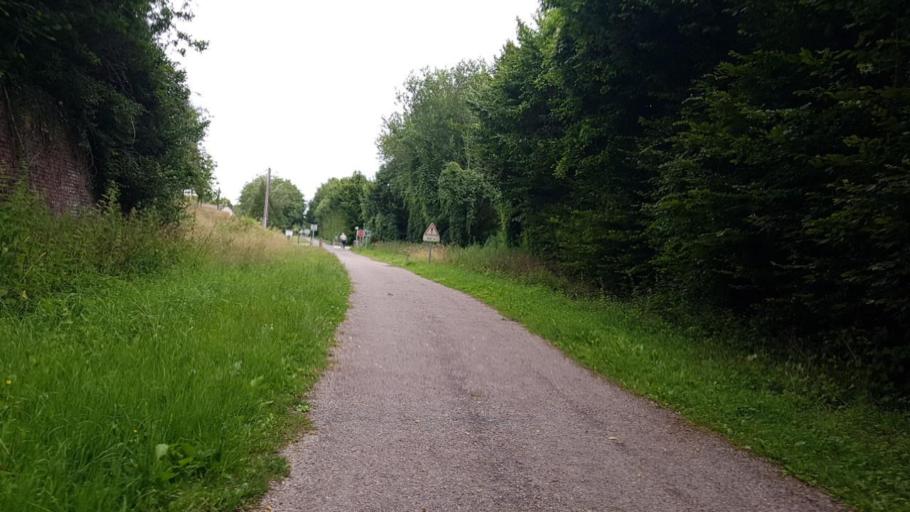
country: FR
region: Picardie
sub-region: Departement de l'Aisne
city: Origny-en-Thierache
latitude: 49.9286
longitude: 4.0299
